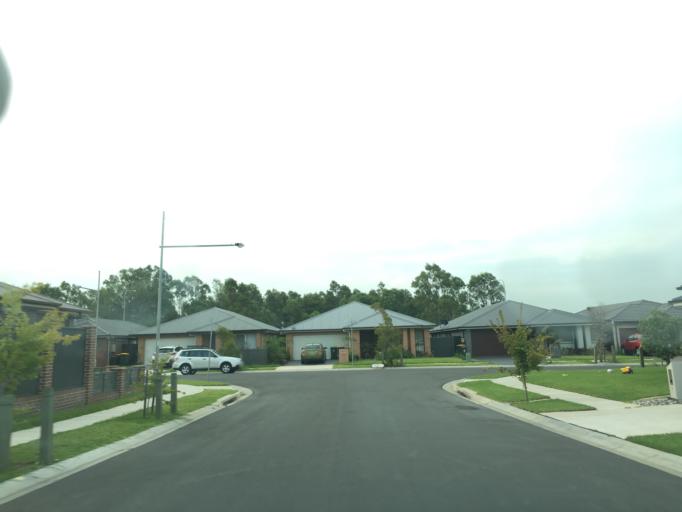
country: AU
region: New South Wales
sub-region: Campbelltown Municipality
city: Denham Court
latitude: -33.9806
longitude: 150.8043
